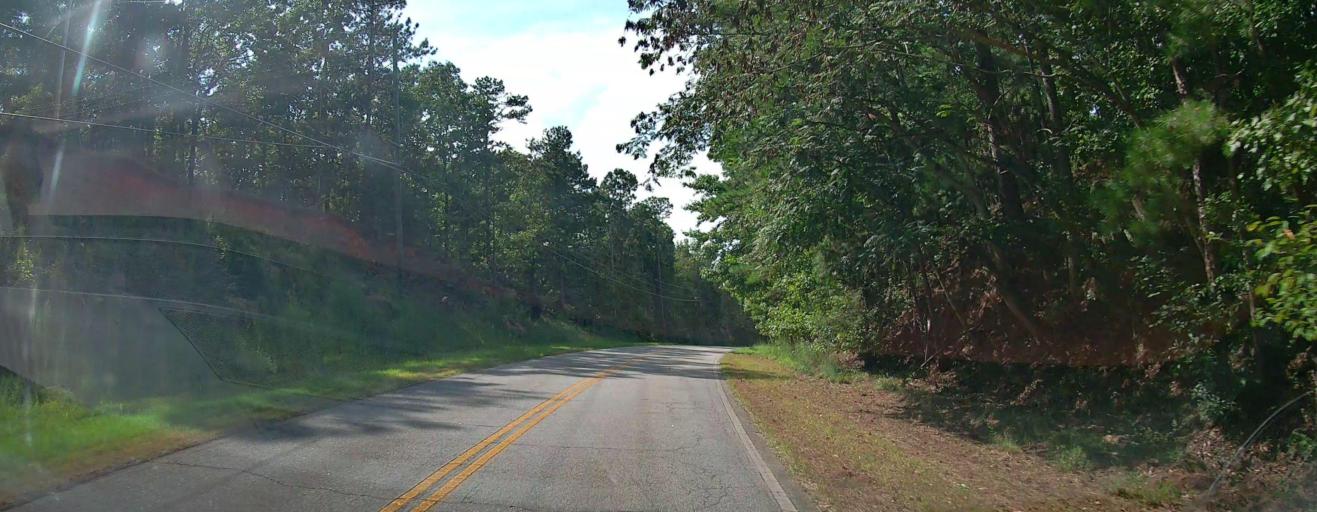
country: US
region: Alabama
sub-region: Russell County
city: Phenix City
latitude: 32.6048
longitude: -84.9768
